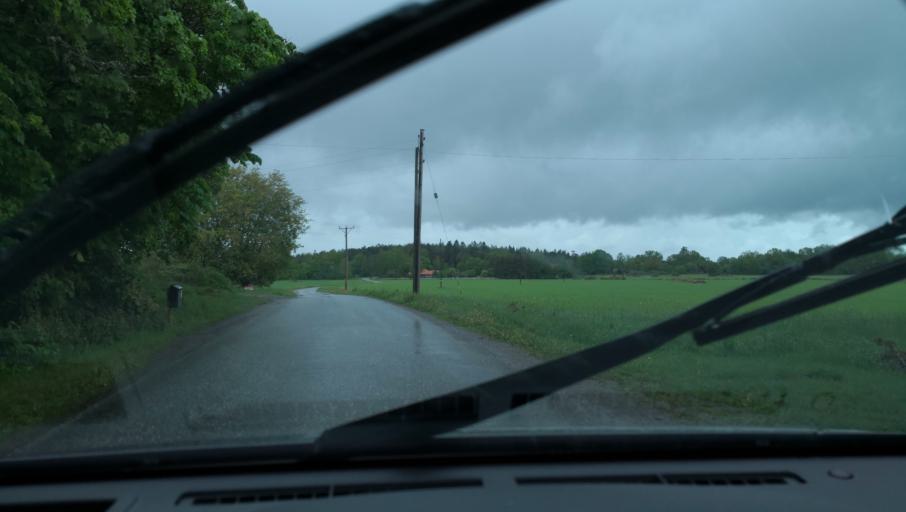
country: SE
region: Uppsala
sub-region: Enkopings Kommun
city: Orsundsbro
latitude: 59.7661
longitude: 17.3419
